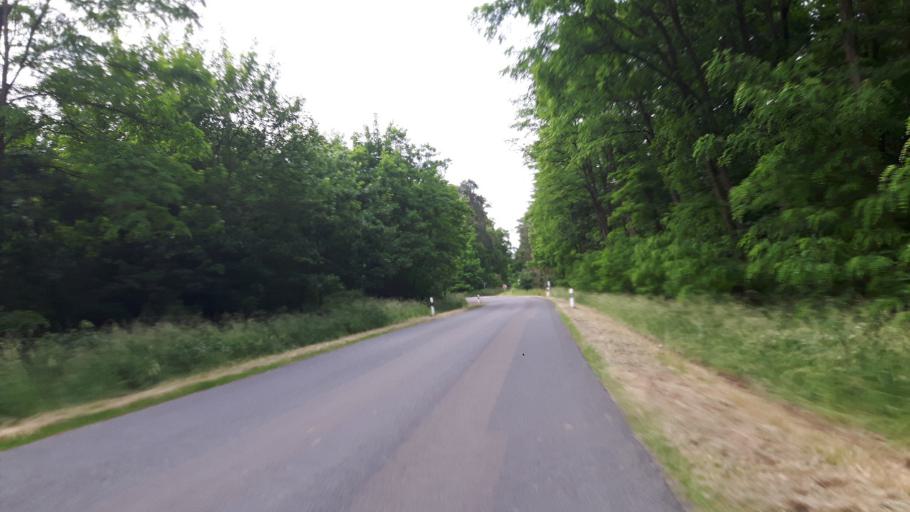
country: DE
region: Saxony-Anhalt
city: Bergwitz
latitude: 51.8228
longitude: 12.5752
